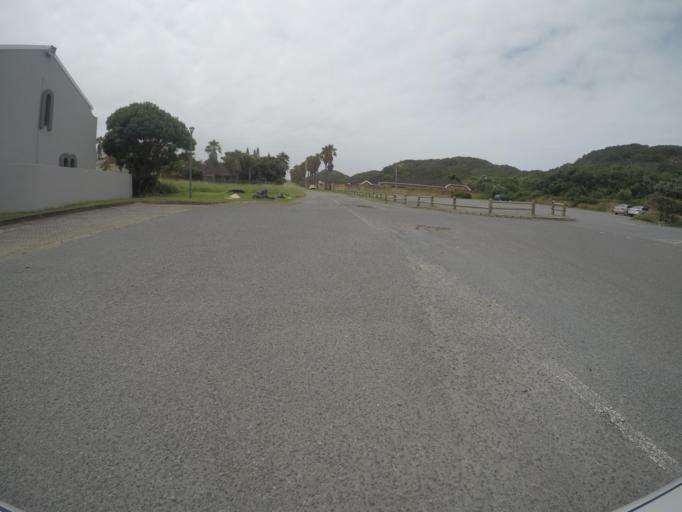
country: ZA
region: Eastern Cape
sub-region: Buffalo City Metropolitan Municipality
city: East London
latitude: -32.9824
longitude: 27.9520
